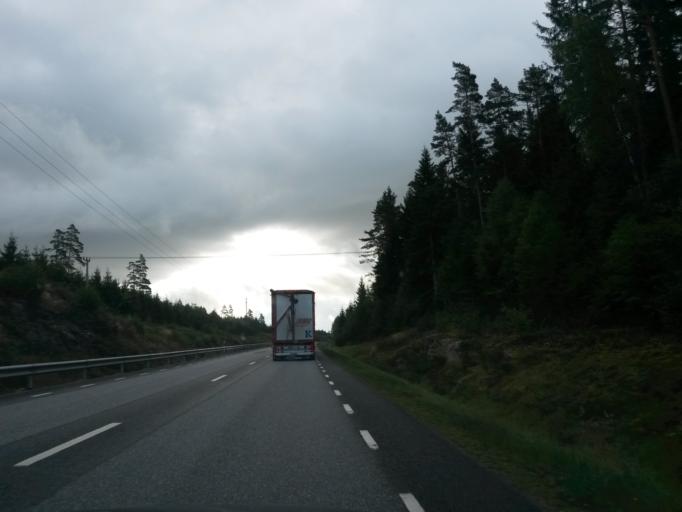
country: SE
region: Vaestra Goetaland
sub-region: Tranemo Kommun
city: Langhem
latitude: 57.6073
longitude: 13.1457
